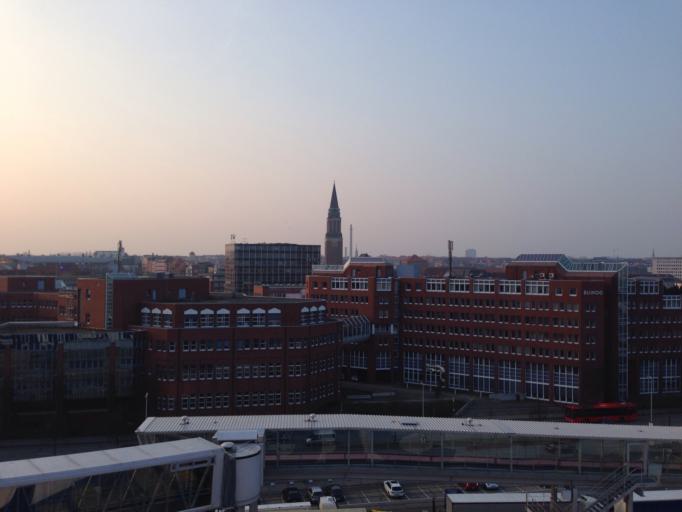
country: DE
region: Schleswig-Holstein
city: Kiel
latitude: 54.3183
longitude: 10.1373
